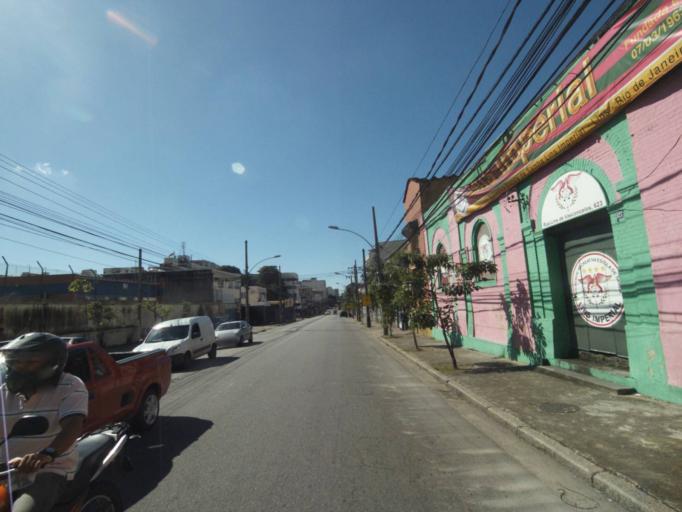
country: BR
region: Rio de Janeiro
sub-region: Rio De Janeiro
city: Rio de Janeiro
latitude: -22.9112
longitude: -43.2852
